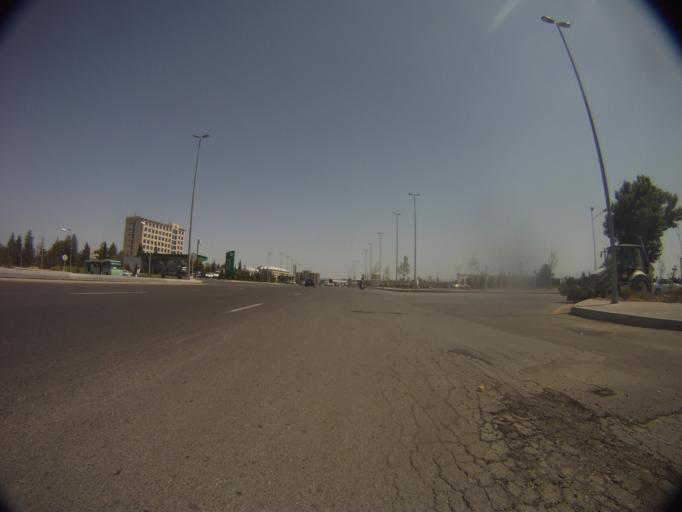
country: AZ
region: Ganja City
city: Ganja
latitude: 40.6890
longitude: 46.3371
